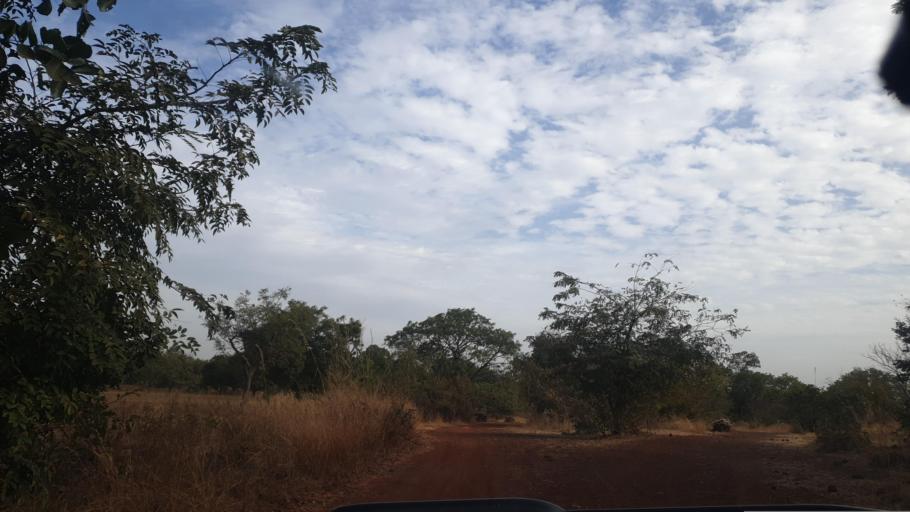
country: ML
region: Sikasso
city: Yanfolila
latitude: 11.4043
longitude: -8.0138
